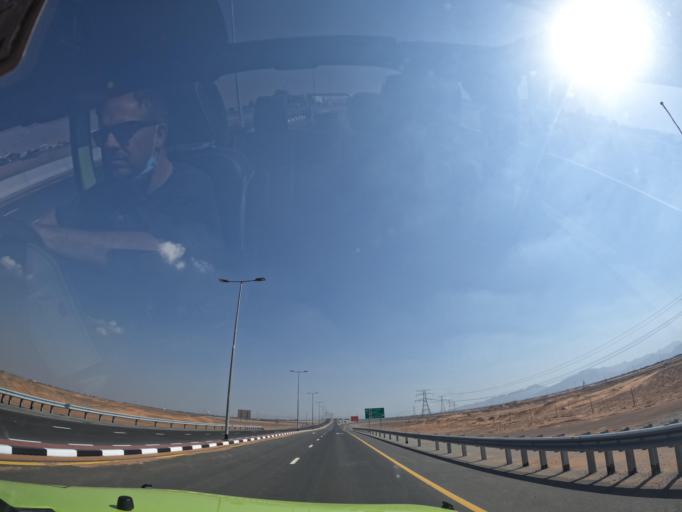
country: AE
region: Ash Shariqah
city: Adh Dhayd
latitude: 24.8114
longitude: 55.7969
